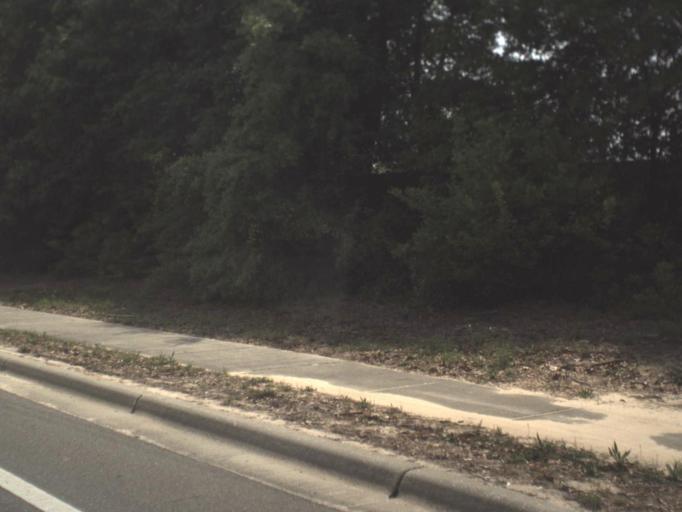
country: US
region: Florida
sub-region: Santa Rosa County
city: Milton
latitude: 30.6256
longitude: -87.0568
